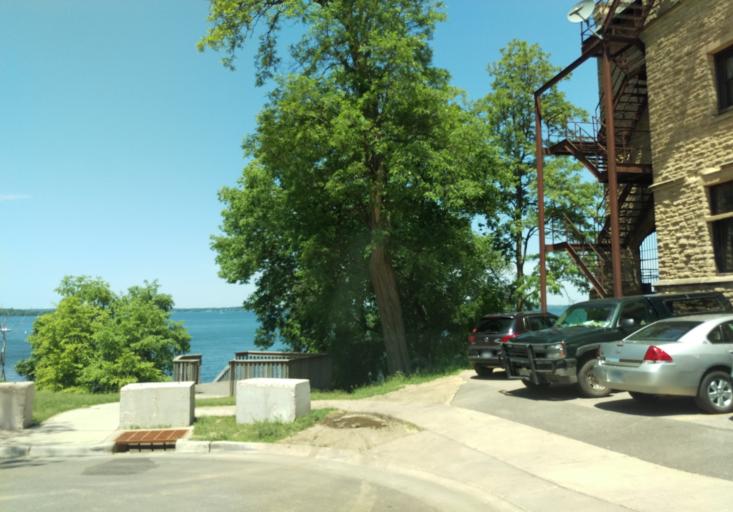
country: US
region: Wisconsin
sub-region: Dane County
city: Madison
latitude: 43.0776
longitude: -89.3935
